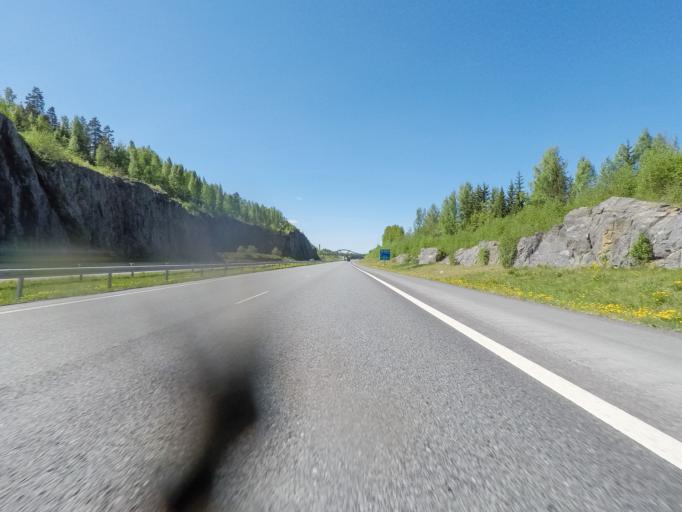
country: FI
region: Pirkanmaa
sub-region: Etelae-Pirkanmaa
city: Akaa
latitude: 61.1784
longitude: 23.9049
